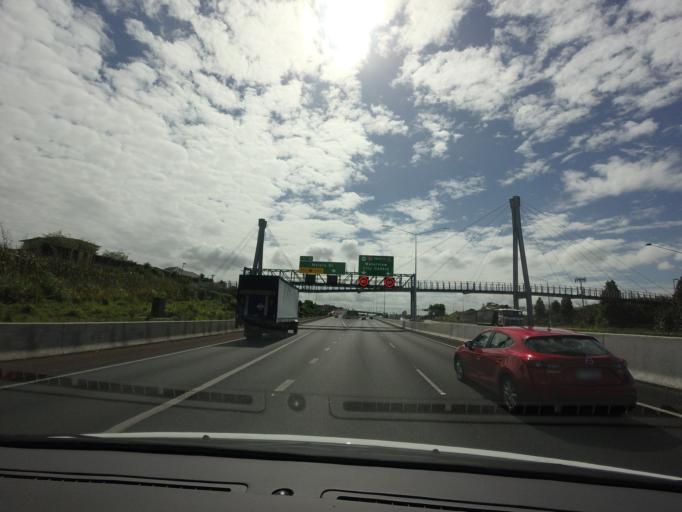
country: NZ
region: Auckland
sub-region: Auckland
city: Auckland
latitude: -36.9062
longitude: 174.7278
